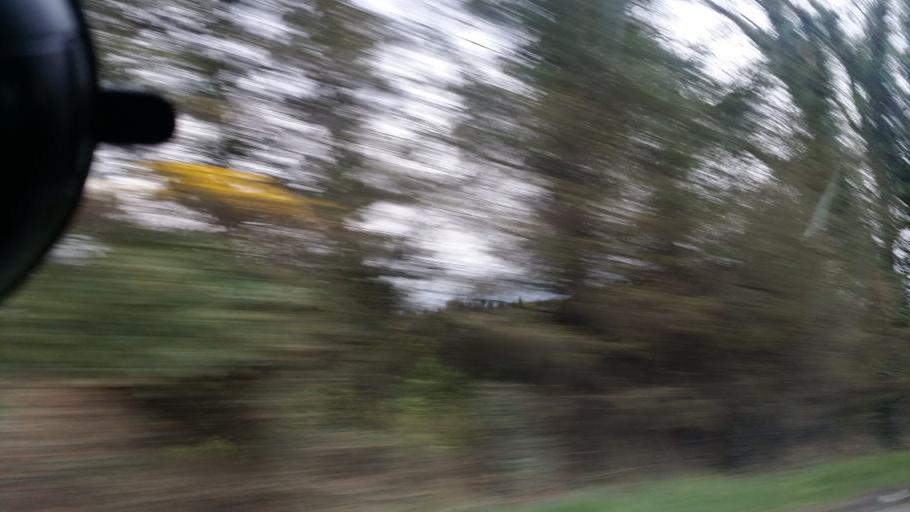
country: IE
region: Ulster
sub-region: An Cabhan
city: Ballyjamesduff
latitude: 53.9379
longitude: -7.2215
